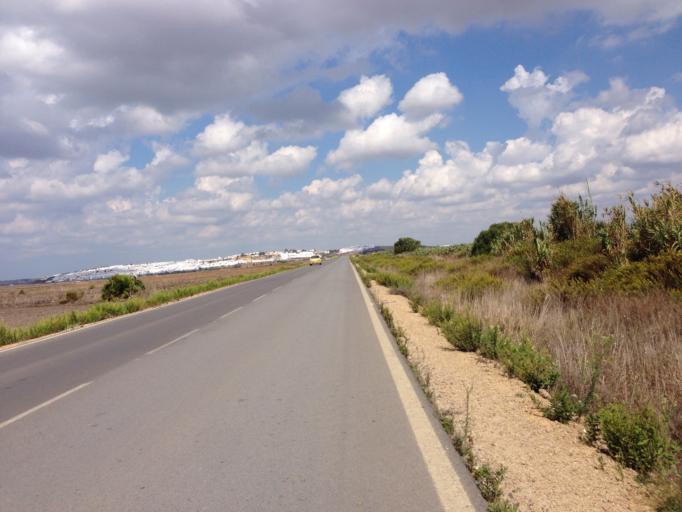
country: ES
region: Andalusia
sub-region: Provincia de Cadiz
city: Conil de la Frontera
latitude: 36.2548
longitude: -6.0698
